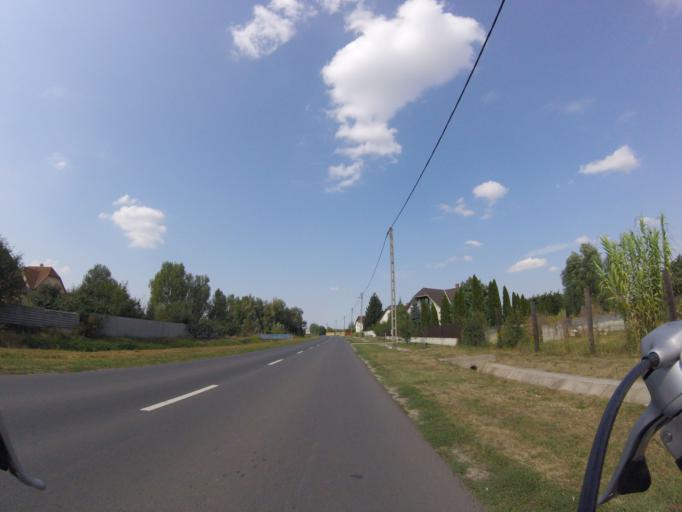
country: HU
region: Szabolcs-Szatmar-Bereg
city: Anarcs
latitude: 48.1786
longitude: 22.1053
